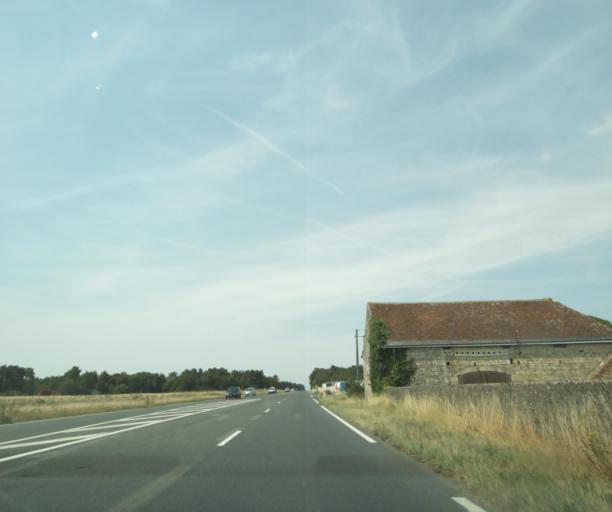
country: FR
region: Centre
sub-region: Departement d'Indre-et-Loire
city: La Celle-Saint-Avant
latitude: 47.0603
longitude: 0.6159
